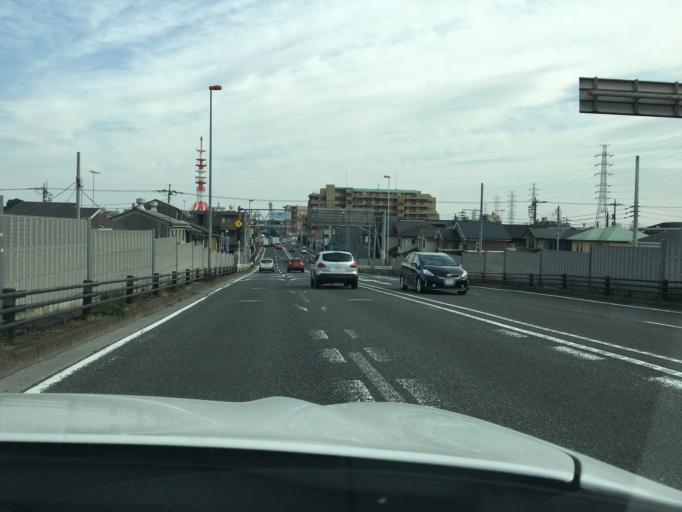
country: JP
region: Saitama
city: Kawagoe
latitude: 35.9047
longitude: 139.4746
